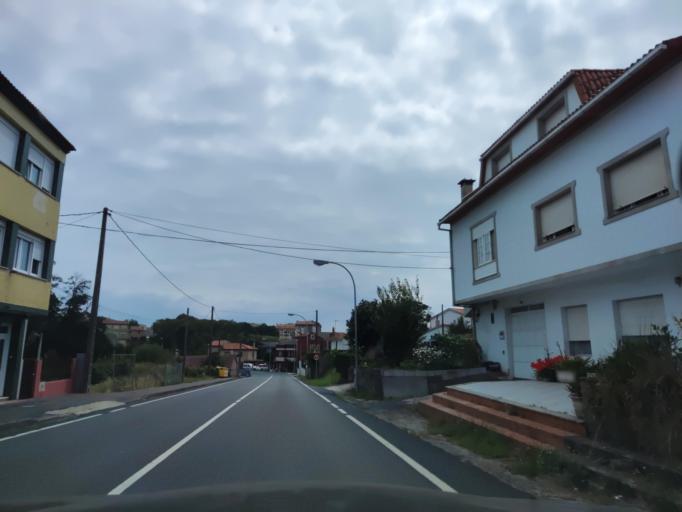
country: ES
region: Galicia
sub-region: Provincia da Coruna
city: Boiro
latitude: 42.6465
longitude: -8.8951
